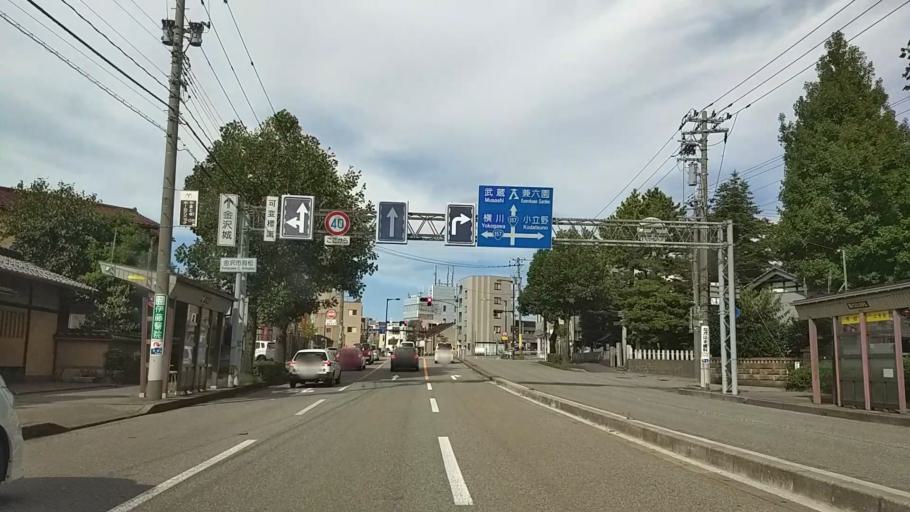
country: JP
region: Ishikawa
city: Nonoichi
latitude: 36.5437
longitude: 136.6407
